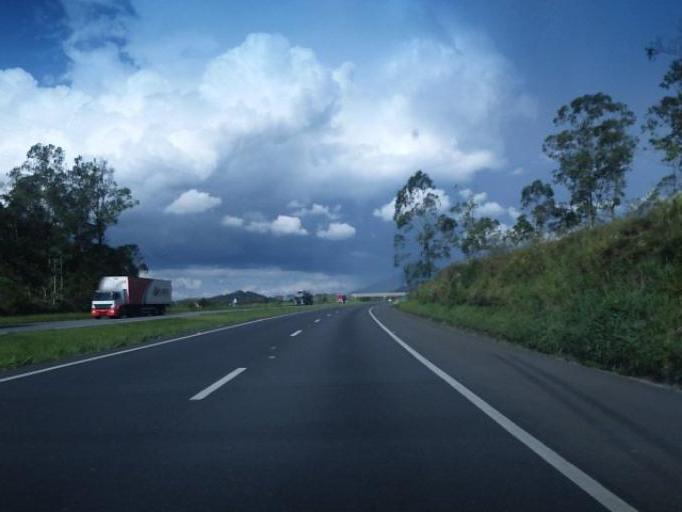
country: BR
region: Sao Paulo
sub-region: Juquia
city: Juquia
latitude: -24.3296
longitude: -47.5797
